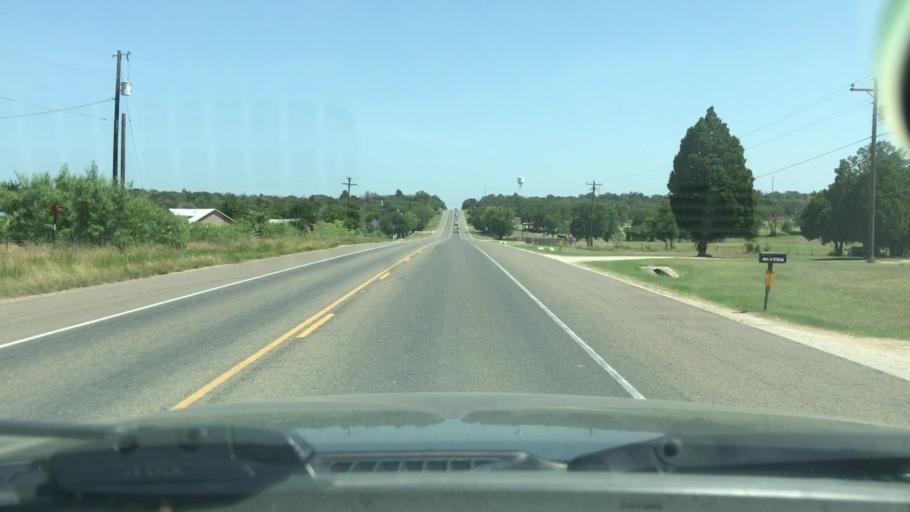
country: US
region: Texas
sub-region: Bastrop County
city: Elgin
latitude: 30.3146
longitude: -97.3540
